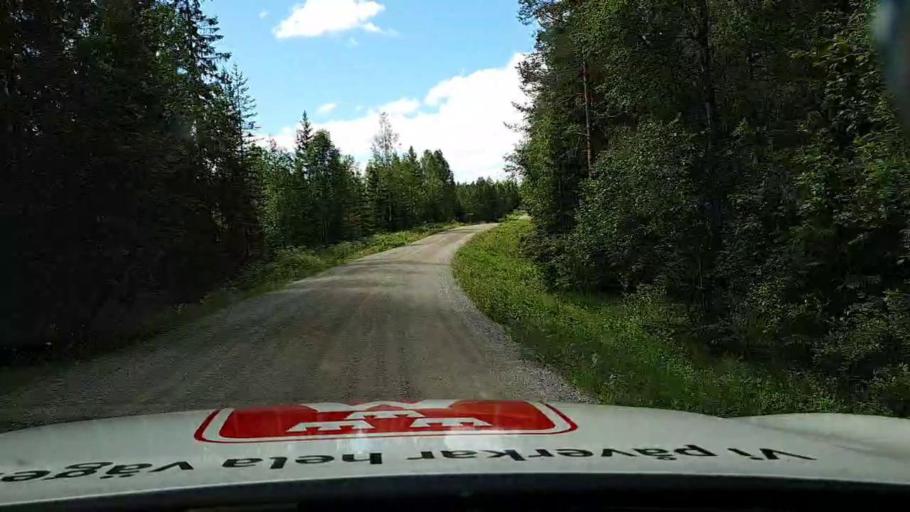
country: SE
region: Jaemtland
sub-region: Braecke Kommun
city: Braecke
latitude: 62.7451
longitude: 15.5022
